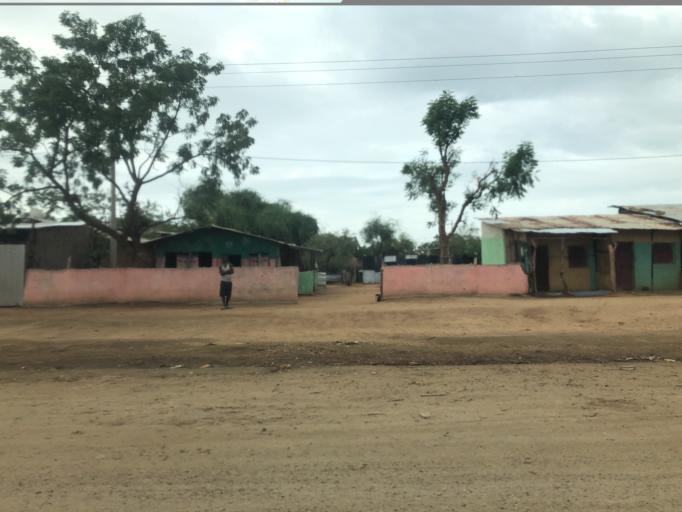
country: ET
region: Southern Nations, Nationalities, and People's Region
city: Turmi
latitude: 4.9697
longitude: 36.4870
